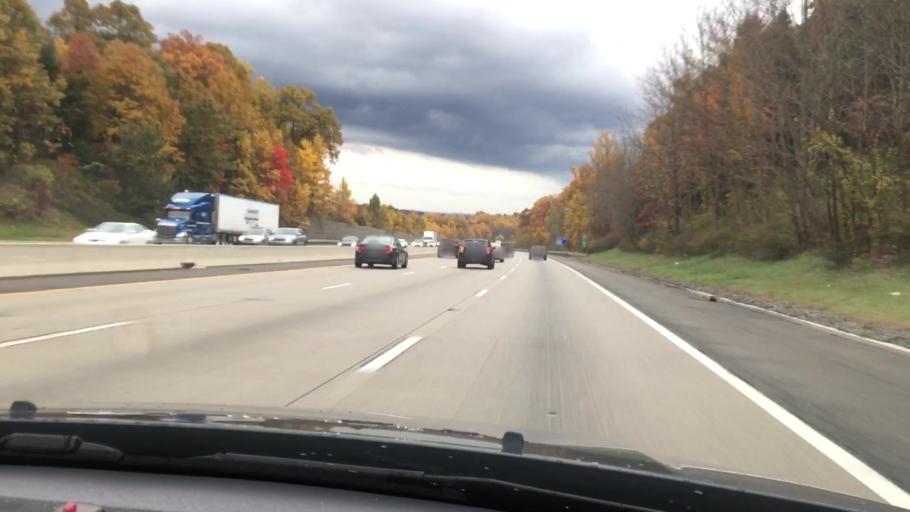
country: US
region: New Jersey
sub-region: Morris County
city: Lincoln Park
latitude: 40.9467
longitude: -74.3454
